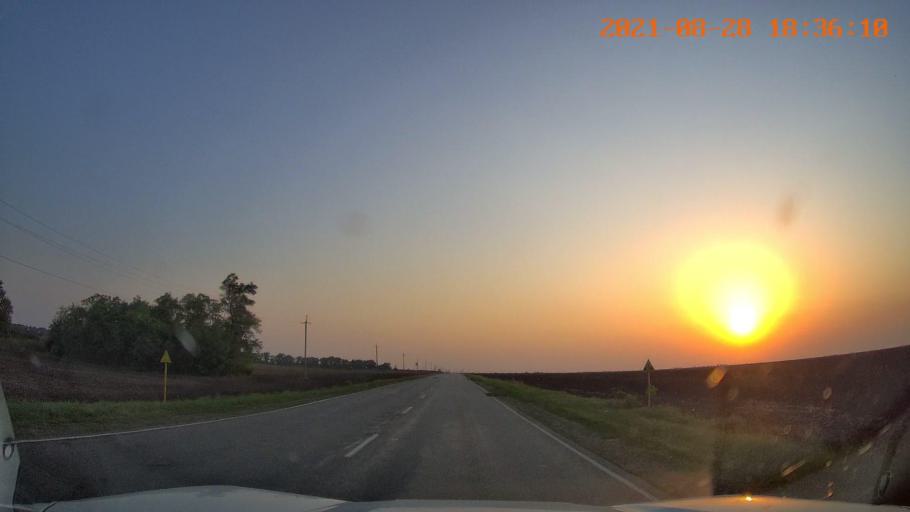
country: RU
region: Adygeya
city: Giaginskaya
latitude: 44.8683
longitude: 40.1179
